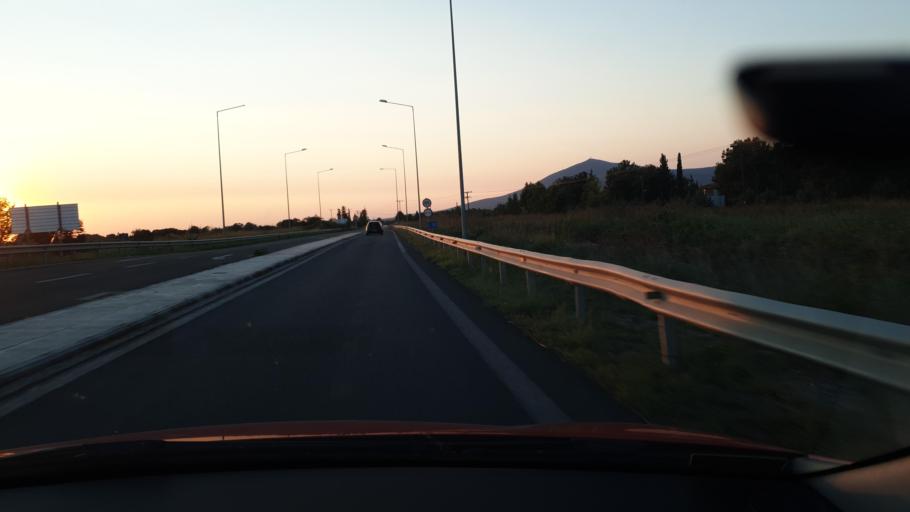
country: GR
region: Central Macedonia
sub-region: Nomos Thessalonikis
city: Vasilika
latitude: 40.4771
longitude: 23.1628
